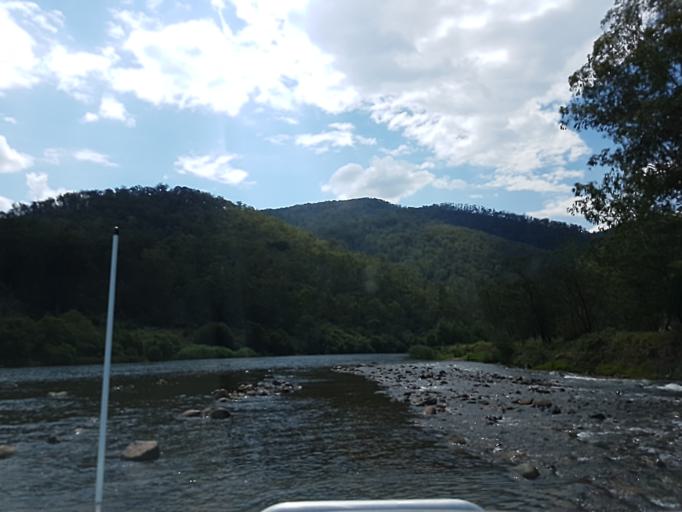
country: AU
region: Victoria
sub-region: East Gippsland
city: Lakes Entrance
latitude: -37.3944
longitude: 148.3340
